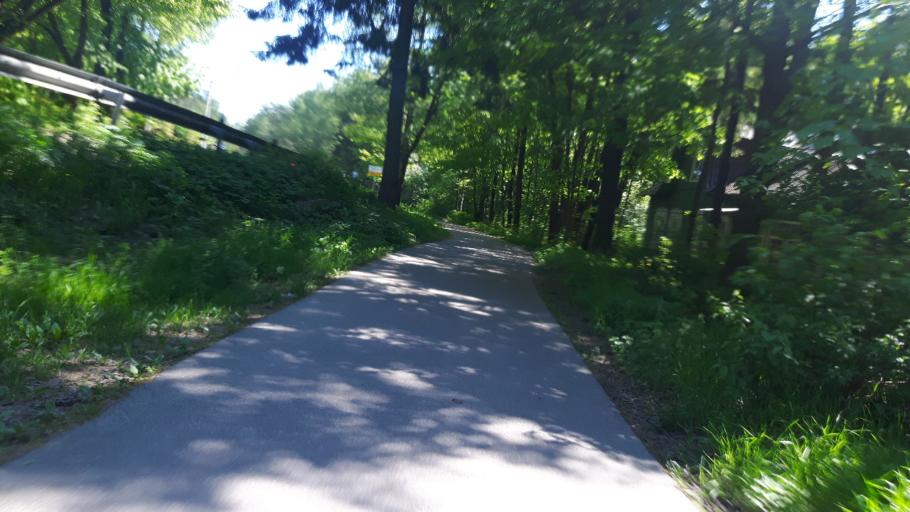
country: RU
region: St.-Petersburg
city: Zelenogorsk
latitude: 60.1925
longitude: 29.6770
